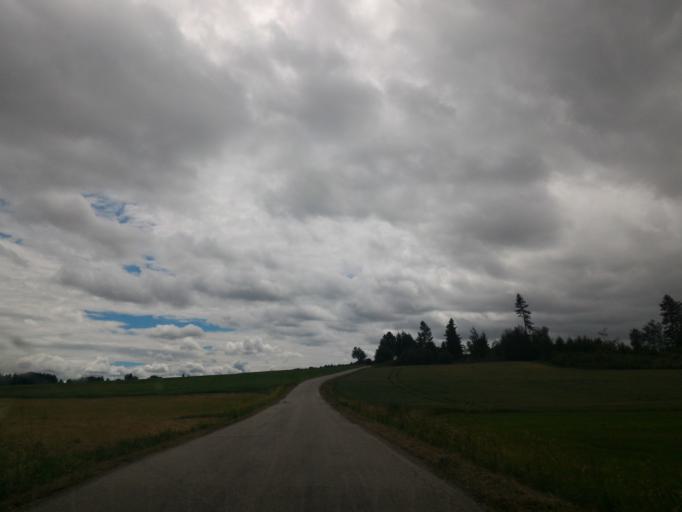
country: CZ
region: Vysocina
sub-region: Okres Jihlava
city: Telc
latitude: 49.2320
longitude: 15.4282
